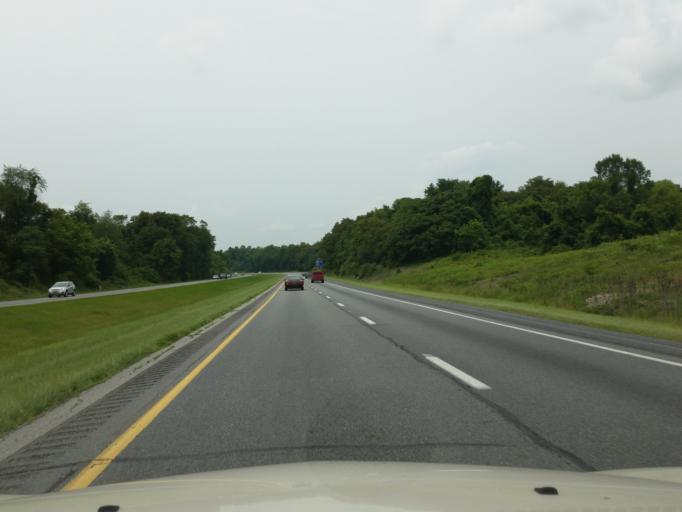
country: US
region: Pennsylvania
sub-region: Dauphin County
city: Middletown
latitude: 40.2164
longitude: -76.7096
